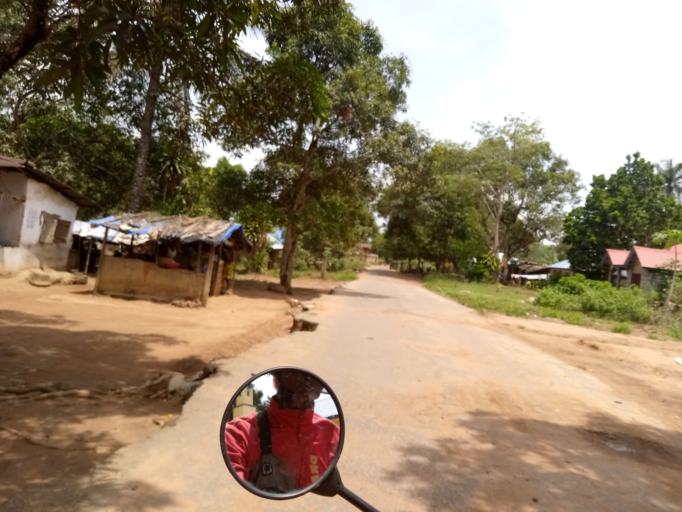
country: SL
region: Western Area
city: Waterloo
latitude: 8.3342
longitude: -13.0140
